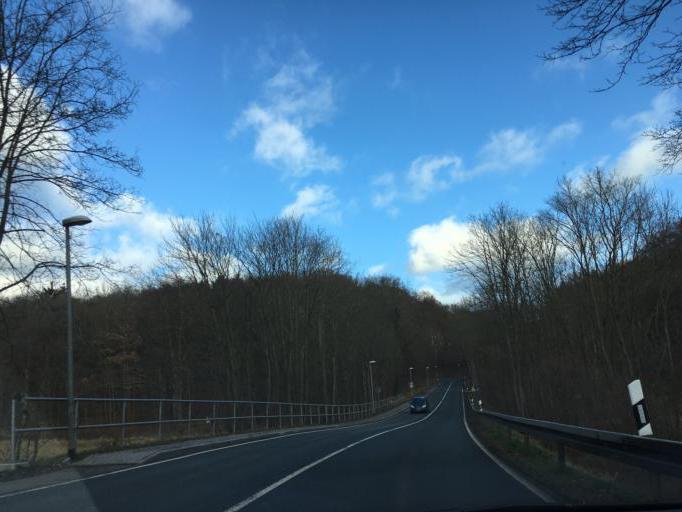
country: DE
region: Thuringia
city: Hetschburg
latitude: 50.9267
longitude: 11.2892
